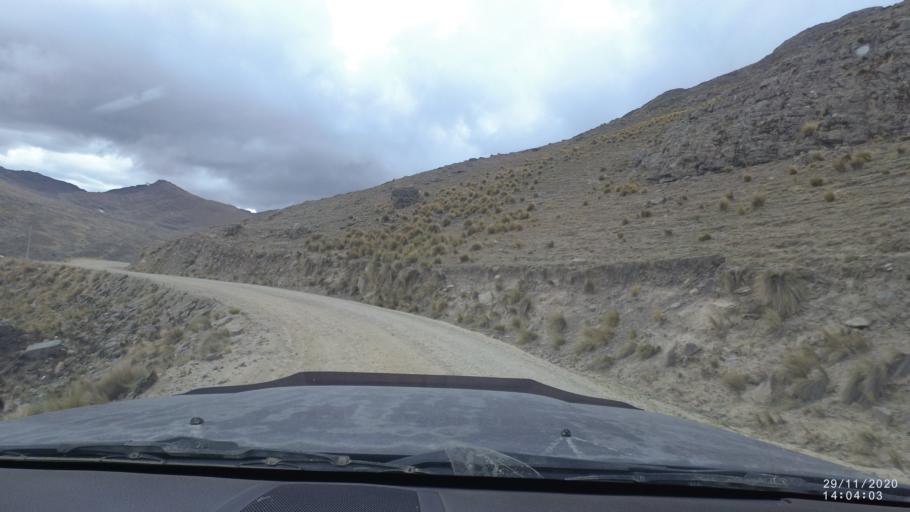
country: BO
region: Cochabamba
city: Sipe Sipe
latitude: -17.1984
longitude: -66.3763
